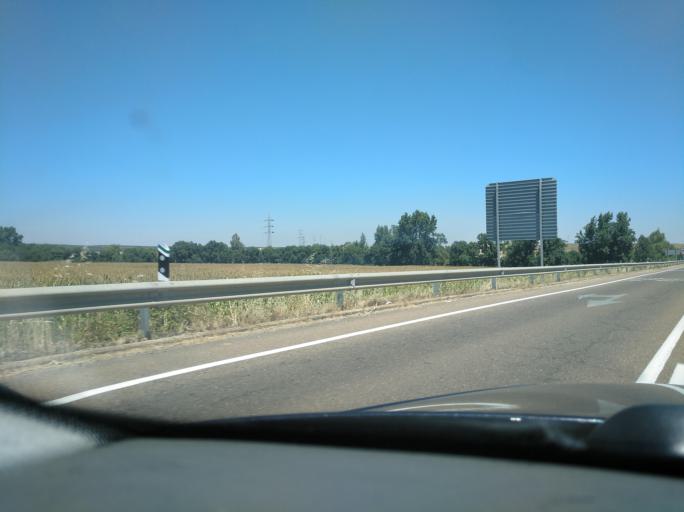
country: ES
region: Extremadura
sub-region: Provincia de Badajoz
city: Olivenza
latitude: 38.7401
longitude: -7.0647
